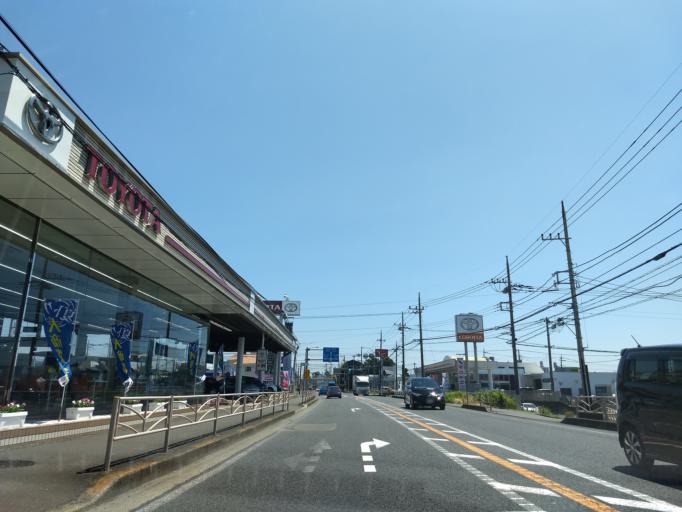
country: JP
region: Kanagawa
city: Isehara
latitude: 35.3985
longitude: 139.2974
